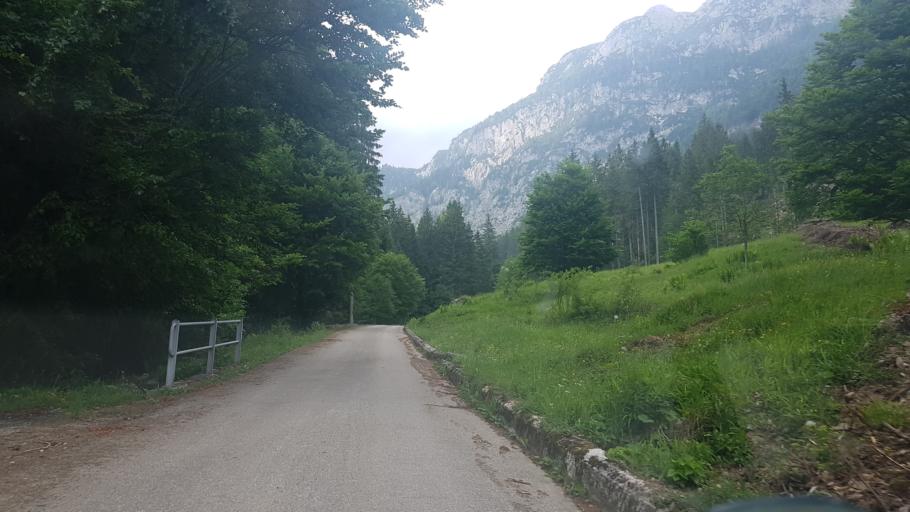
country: IT
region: Friuli Venezia Giulia
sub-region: Provincia di Udine
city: Paularo
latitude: 46.5398
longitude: 13.2053
